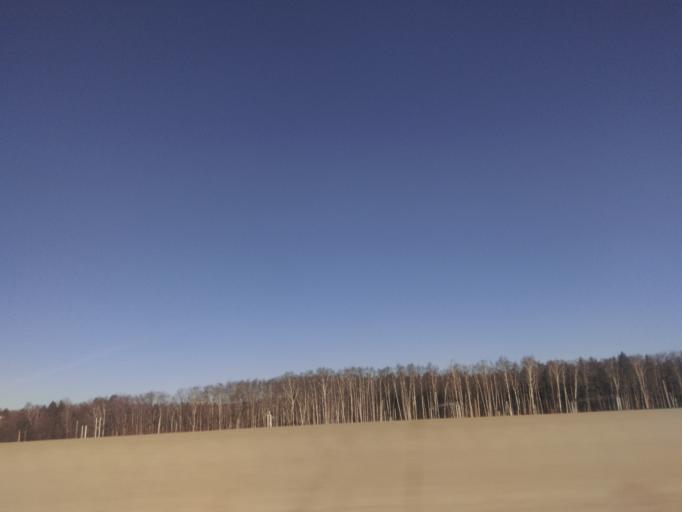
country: RU
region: Moskovskaya
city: Novoivanovskoye
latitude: 55.7005
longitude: 37.3474
